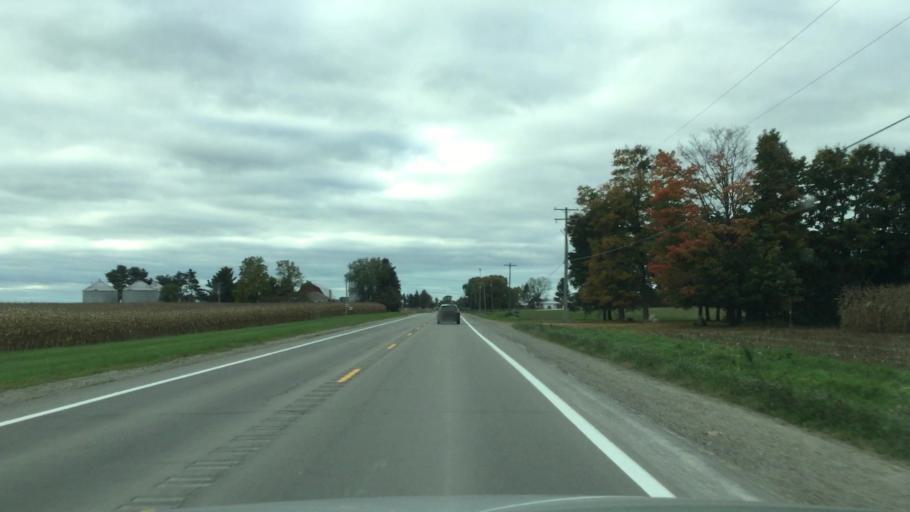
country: US
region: Michigan
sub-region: Macomb County
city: Memphis
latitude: 42.8732
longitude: -82.7677
